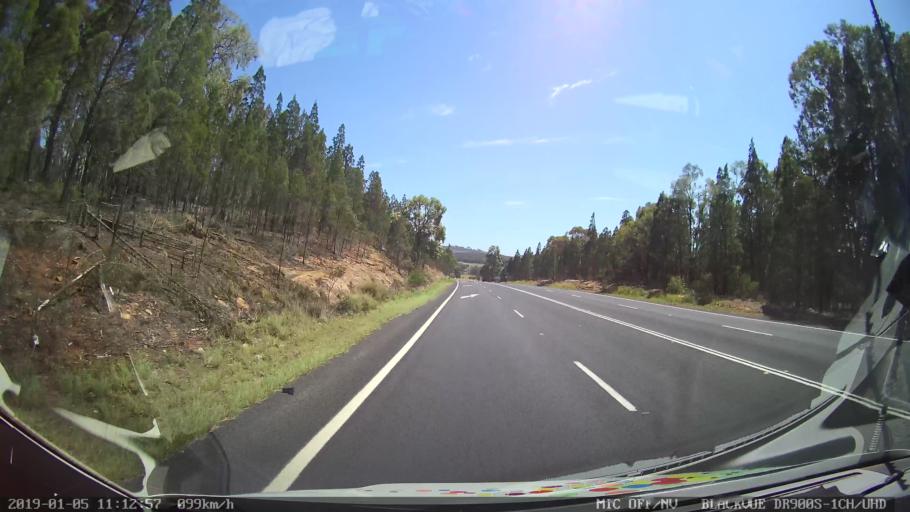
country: AU
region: New South Wales
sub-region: Warrumbungle Shire
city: Coonabarabran
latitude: -31.3765
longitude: 149.2660
